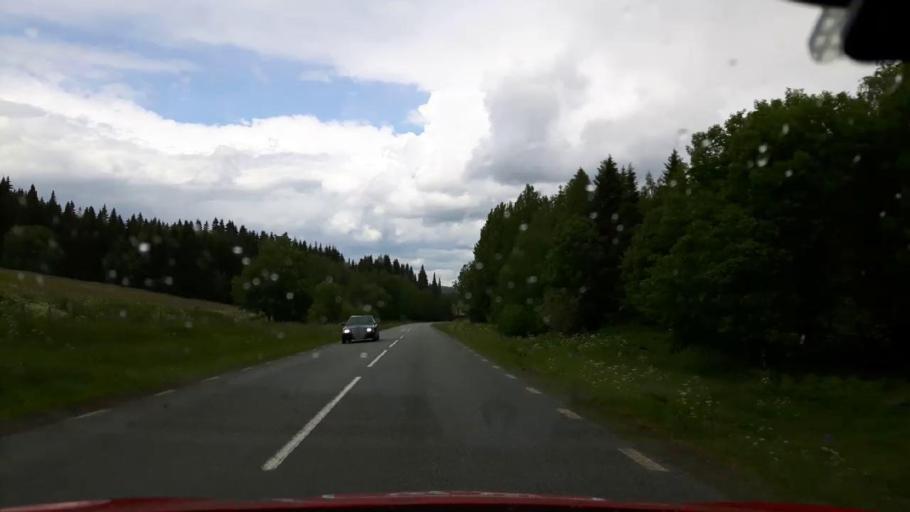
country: SE
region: Jaemtland
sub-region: Krokoms Kommun
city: Krokom
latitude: 63.4975
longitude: 14.2136
